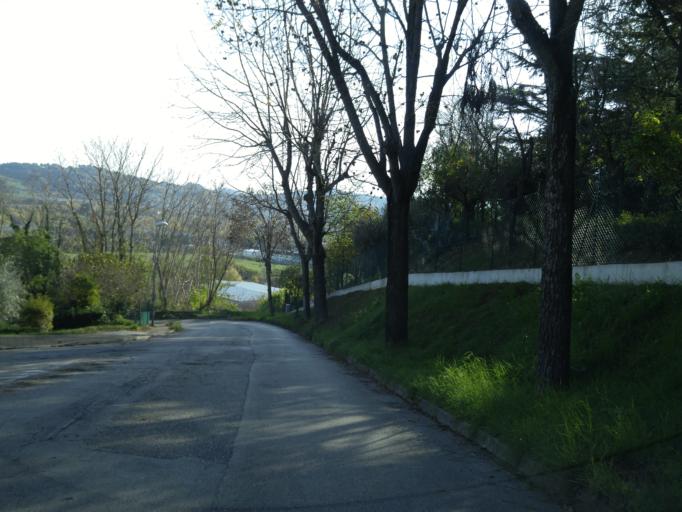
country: IT
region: The Marches
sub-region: Provincia di Pesaro e Urbino
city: Calcinelli
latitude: 43.7496
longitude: 12.9123
